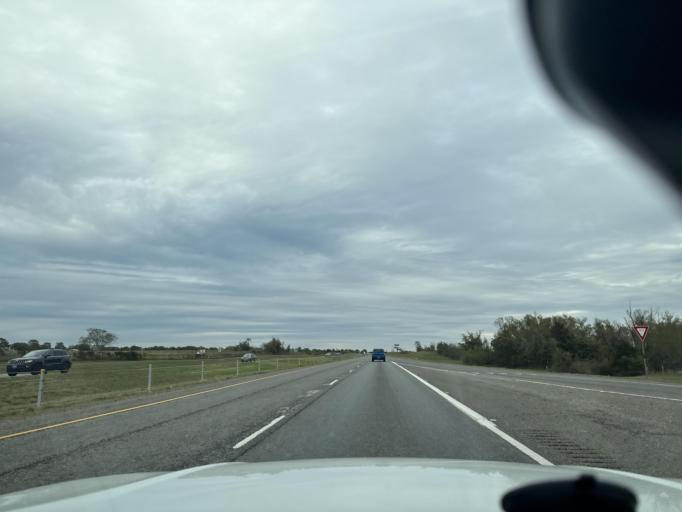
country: US
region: Texas
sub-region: Burleson County
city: Somerville
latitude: 30.1538
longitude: -96.6261
